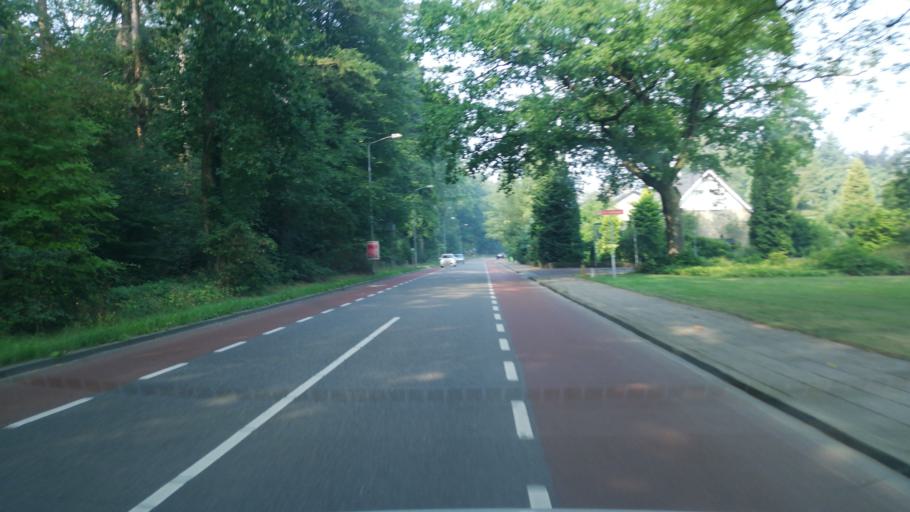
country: NL
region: Gelderland
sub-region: Gemeente Ermelo
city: Ermelo
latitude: 52.2920
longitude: 5.6332
